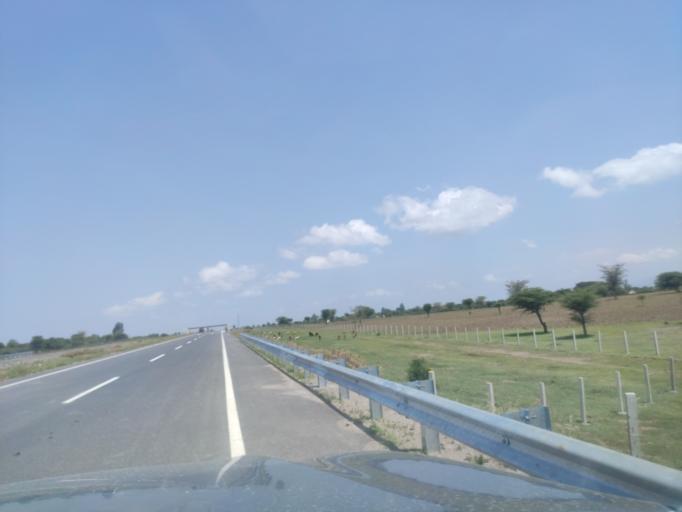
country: ET
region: Oromiya
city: Ziway
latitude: 8.2554
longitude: 38.8939
